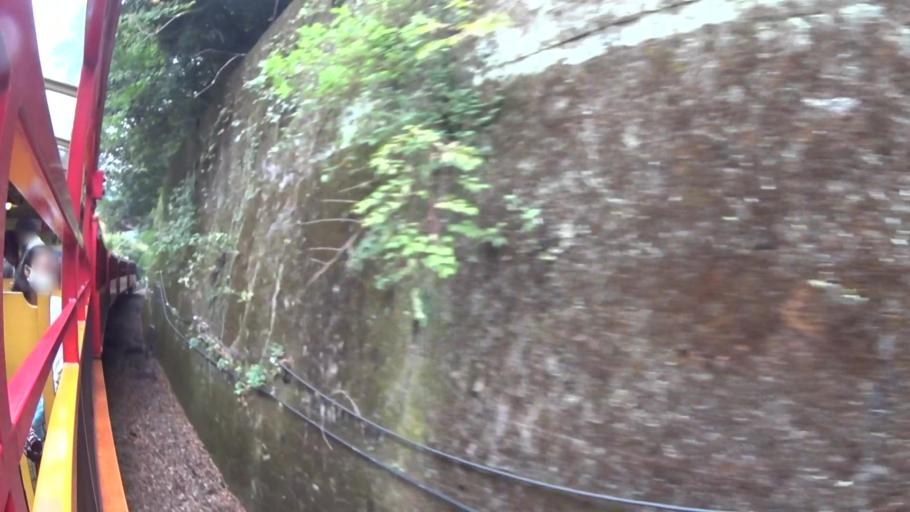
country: JP
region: Kyoto
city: Muko
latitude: 35.0214
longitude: 135.6556
